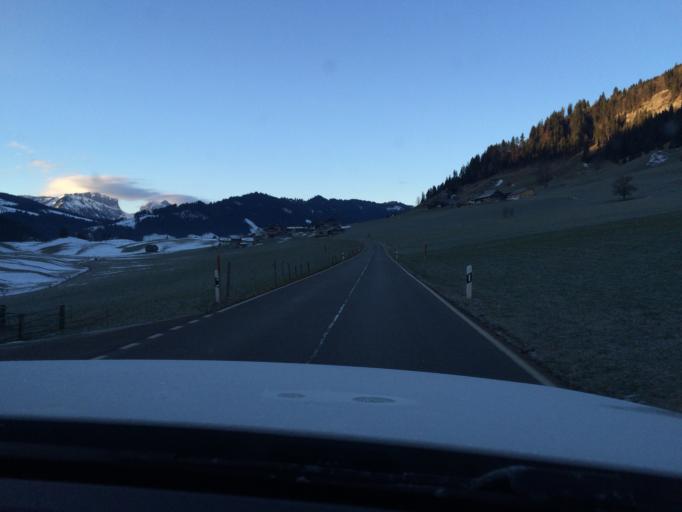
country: CH
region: Bern
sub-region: Emmental District
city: Wald
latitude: 46.8398
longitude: 7.8817
